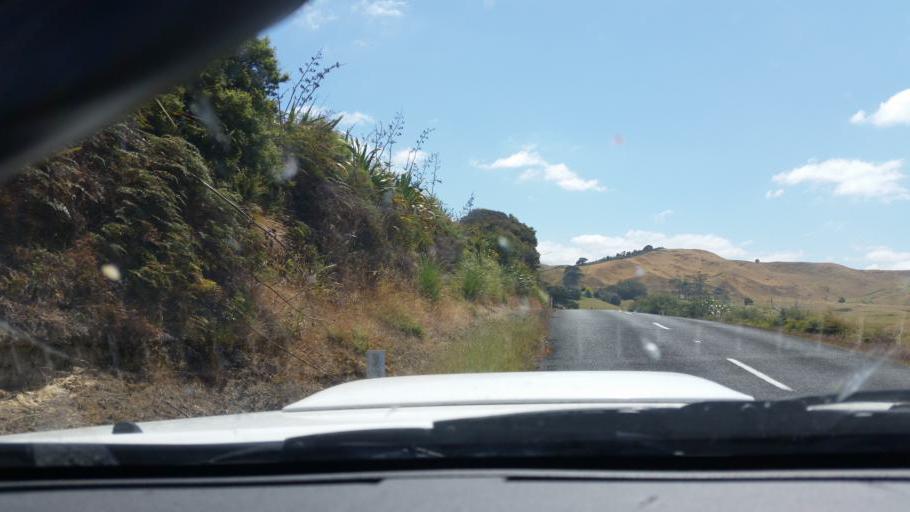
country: NZ
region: Northland
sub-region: Kaipara District
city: Dargaville
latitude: -35.8270
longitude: 173.6731
